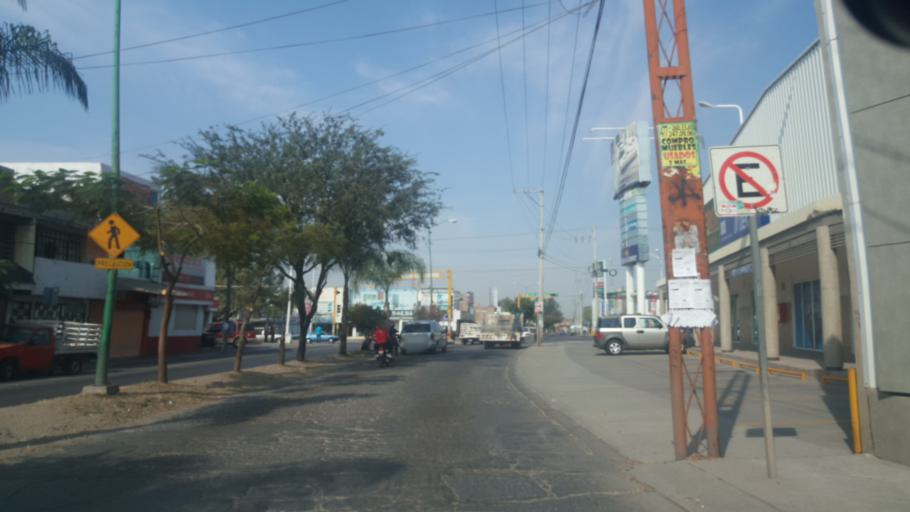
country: MX
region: Guanajuato
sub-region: Leon
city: Fraccionamiento Paraiso Real
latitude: 21.1012
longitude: -101.6125
